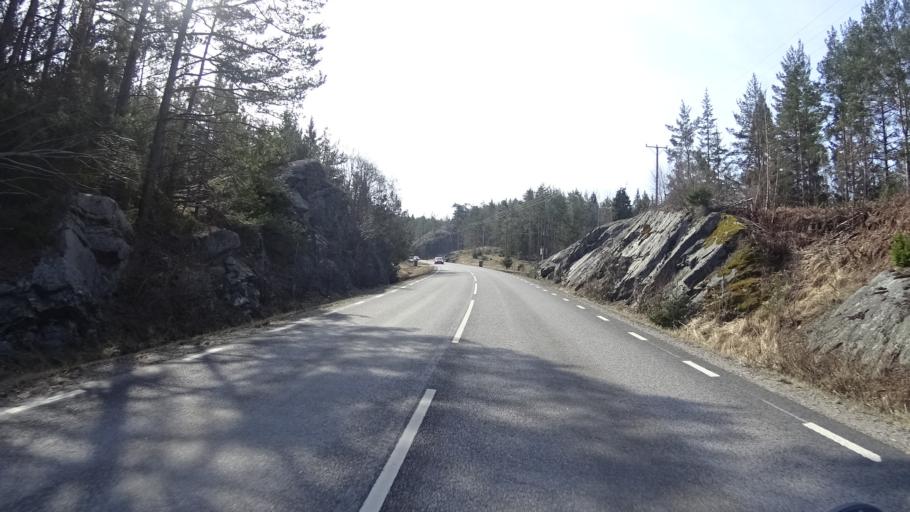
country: SE
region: Stockholm
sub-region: Nynashamns Kommun
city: Nynashamn
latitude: 58.9555
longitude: 17.9971
